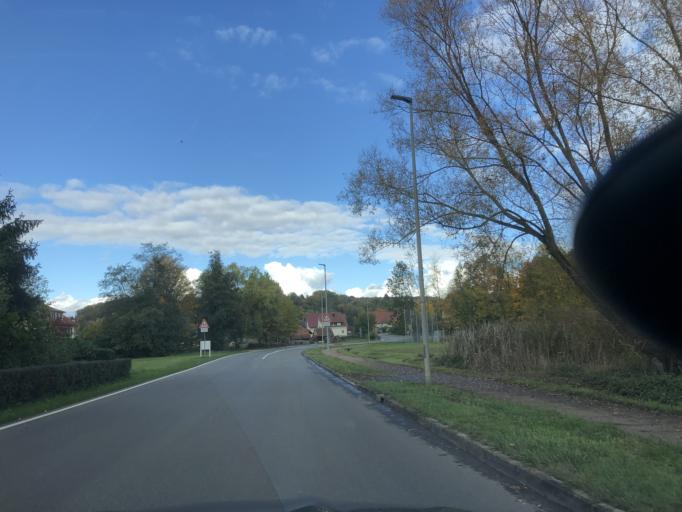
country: DE
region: Baden-Wuerttemberg
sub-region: Regierungsbezirk Stuttgart
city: Winterbach
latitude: 48.8451
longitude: 9.4535
